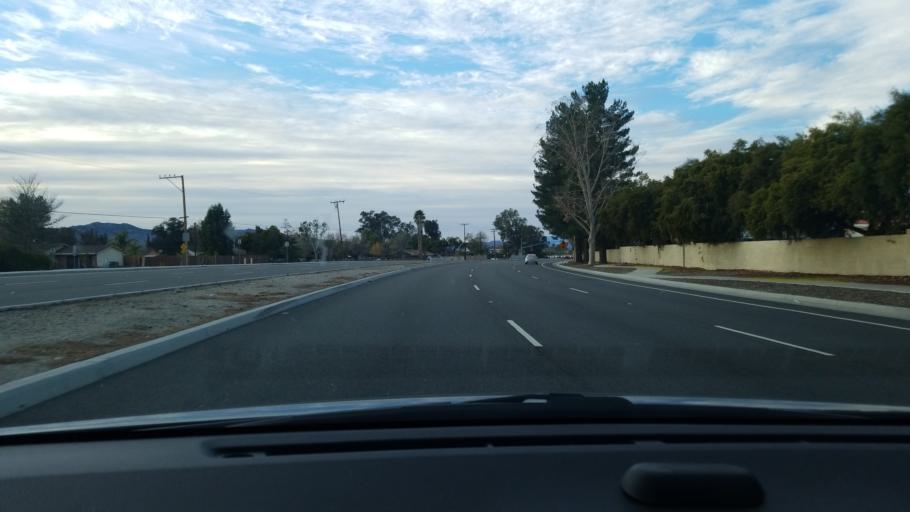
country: US
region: California
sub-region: Riverside County
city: San Jacinto
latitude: 33.8025
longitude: -116.9745
